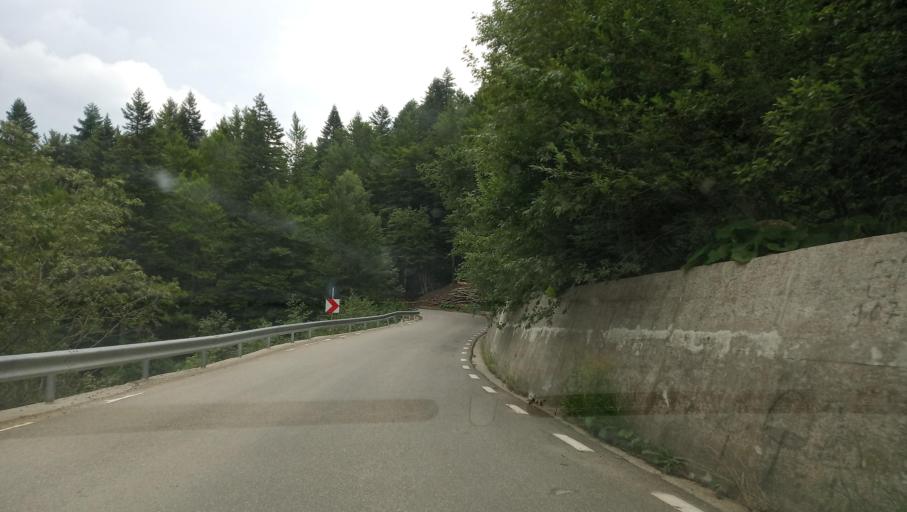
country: RO
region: Prahova
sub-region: Oras Sinaia
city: Sinaia
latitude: 45.3240
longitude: 25.5040
